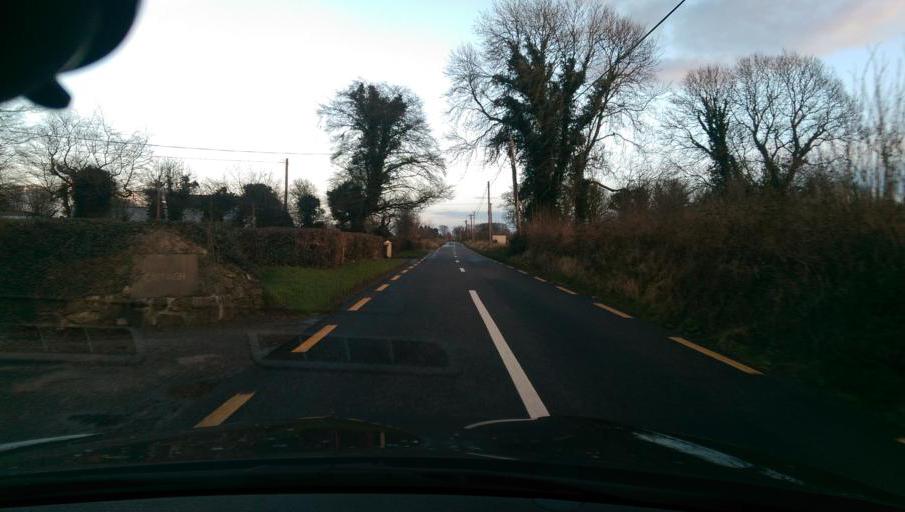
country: IE
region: Connaught
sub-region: County Galway
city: Ballinasloe
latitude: 53.3875
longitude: -8.3077
